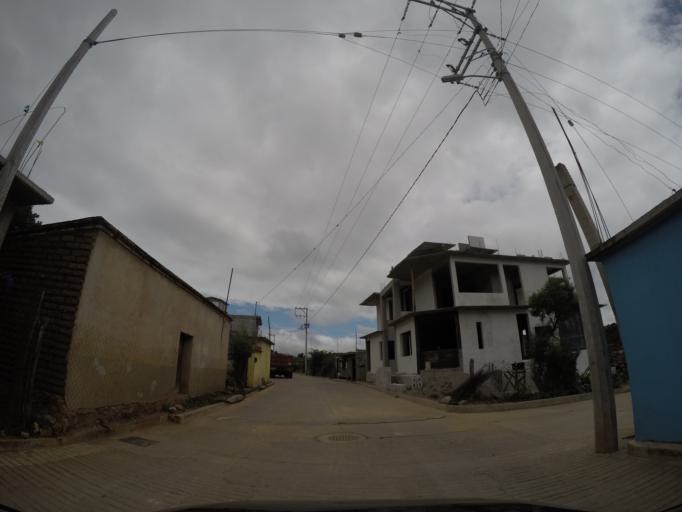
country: MX
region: Oaxaca
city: San Lorenzo Albarradas
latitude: 16.9097
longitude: -96.2580
